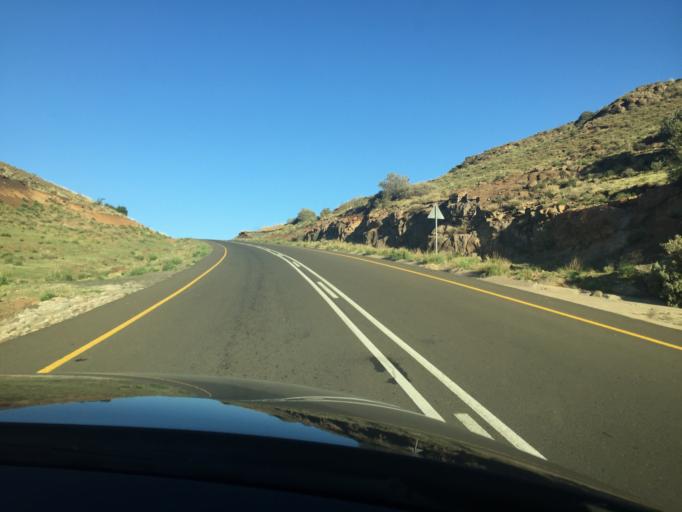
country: LS
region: Maseru
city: Nako
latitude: -29.6568
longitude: 27.8606
